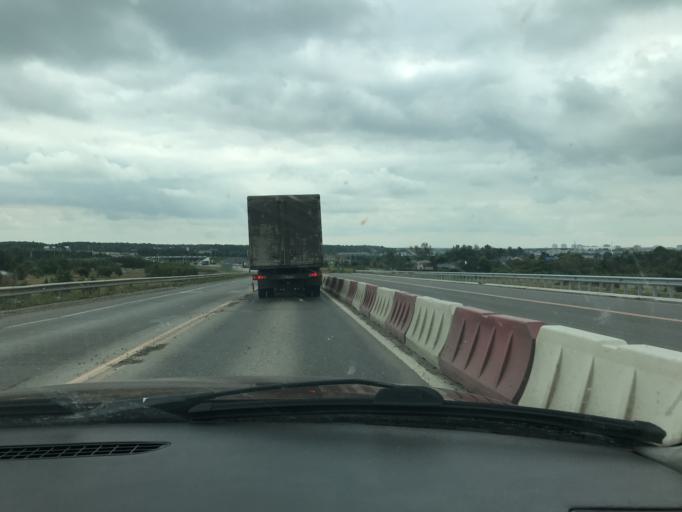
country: RU
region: Kaluga
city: Kaluga
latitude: 54.5610
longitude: 36.3353
